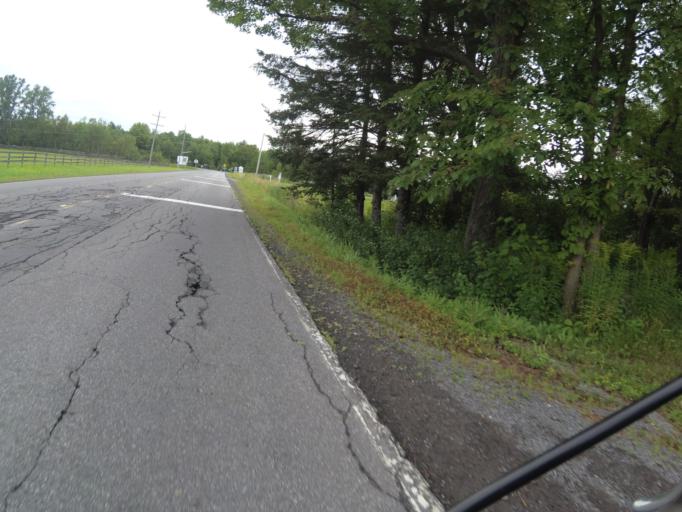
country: CA
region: Ontario
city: Bourget
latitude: 45.3523
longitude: -75.2814
